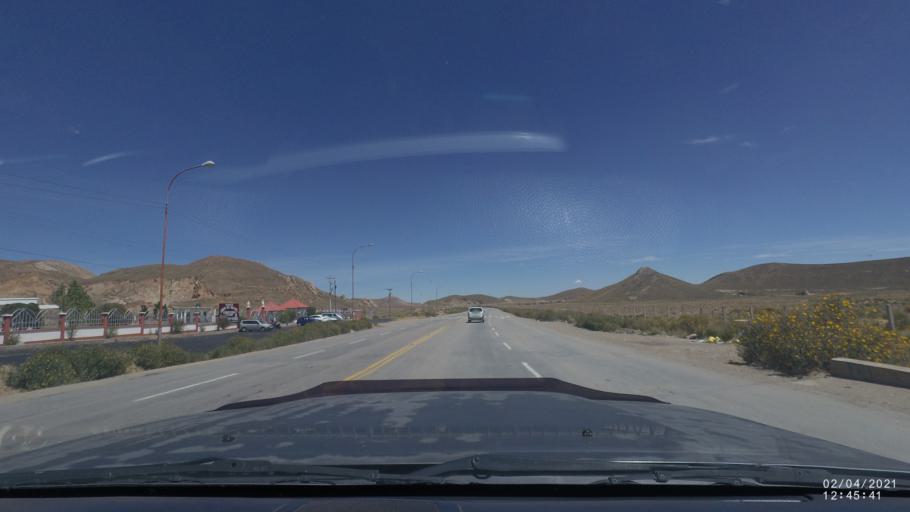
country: BO
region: Oruro
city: Oruro
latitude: -17.9377
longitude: -67.1355
